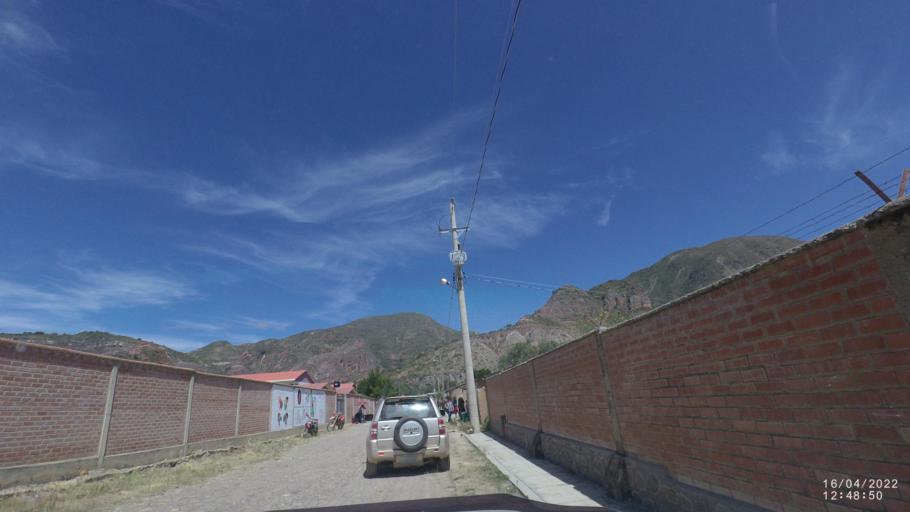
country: BO
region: Cochabamba
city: Mizque
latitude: -17.9865
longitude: -65.6287
